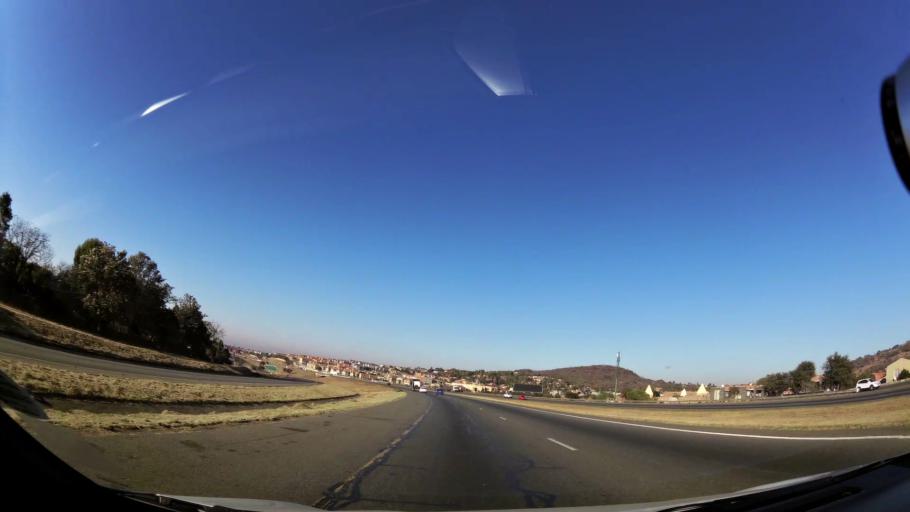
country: ZA
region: Gauteng
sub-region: Ekurhuleni Metropolitan Municipality
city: Germiston
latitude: -26.2833
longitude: 28.1016
